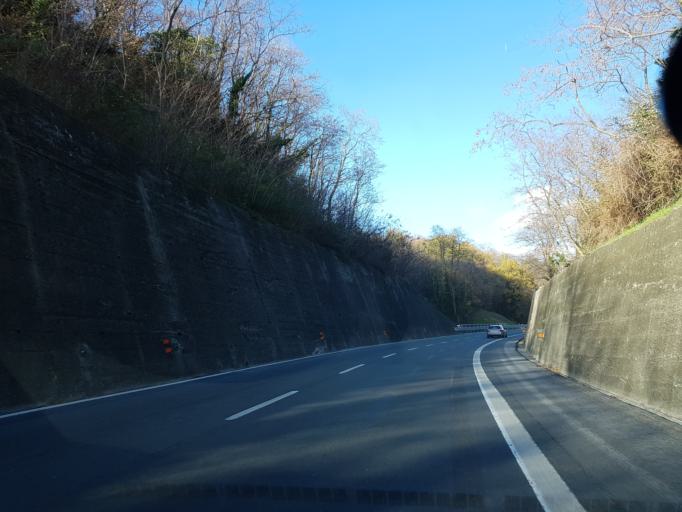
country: IT
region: Liguria
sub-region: Provincia di Genova
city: Manesseno
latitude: 44.4876
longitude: 8.9162
